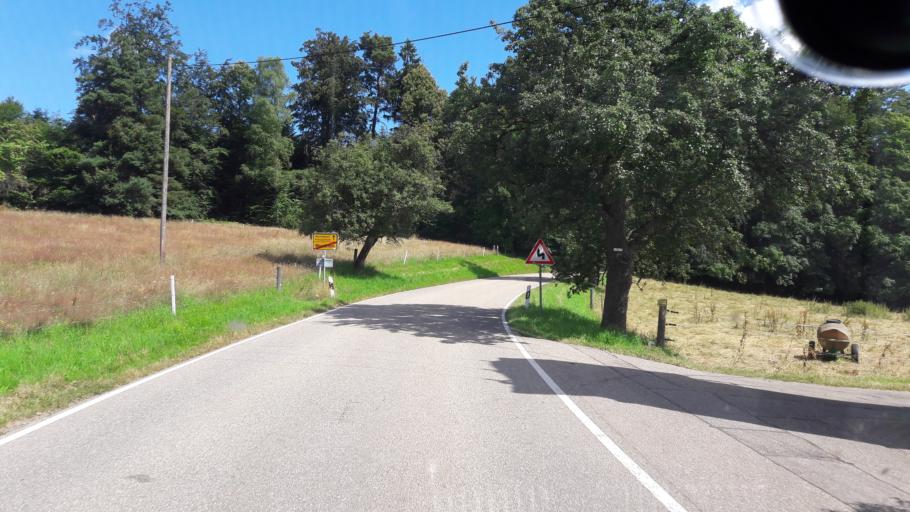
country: DE
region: Baden-Wuerttemberg
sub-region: Karlsruhe Region
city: Bad Herrenalb
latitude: 48.8394
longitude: 8.3871
